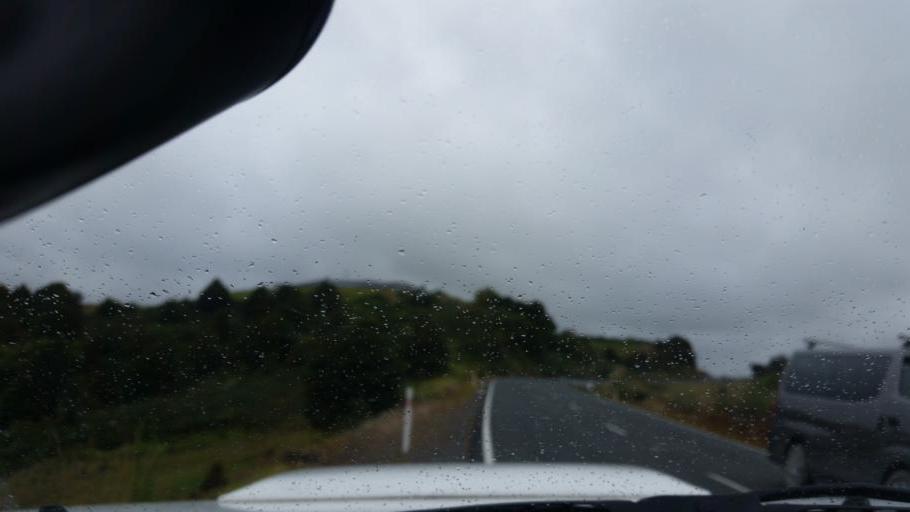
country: NZ
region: Auckland
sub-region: Auckland
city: Wellsford
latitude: -36.1342
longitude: 174.5273
